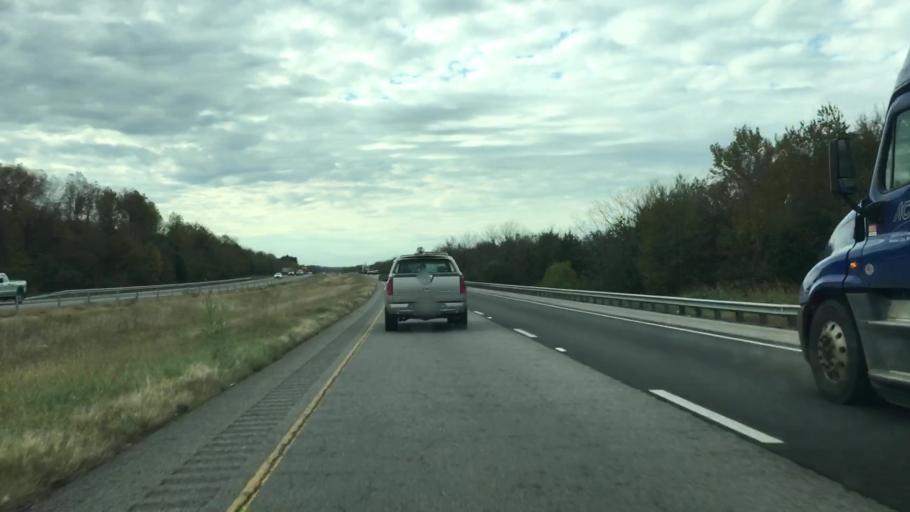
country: US
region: Arkansas
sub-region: Conway County
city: Morrilton
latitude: 35.1634
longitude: -92.6228
